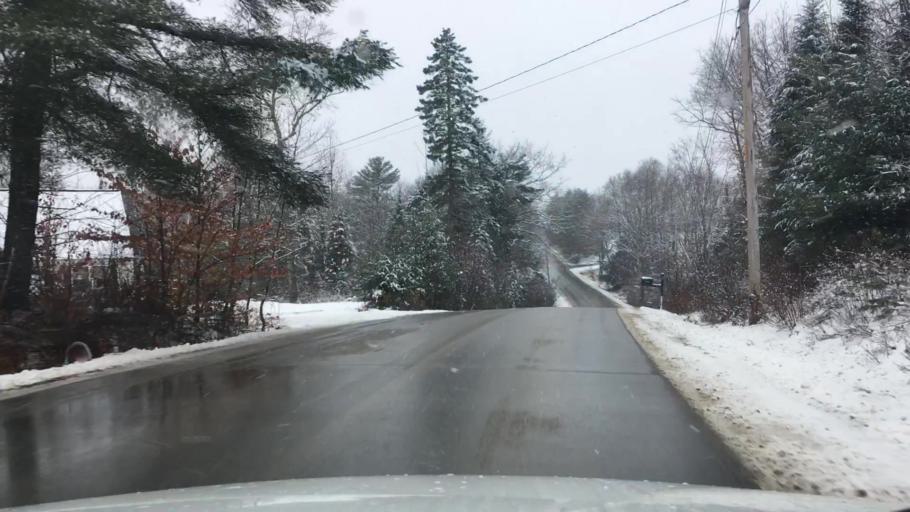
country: US
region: Maine
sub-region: Knox County
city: Union
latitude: 44.1583
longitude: -69.2976
